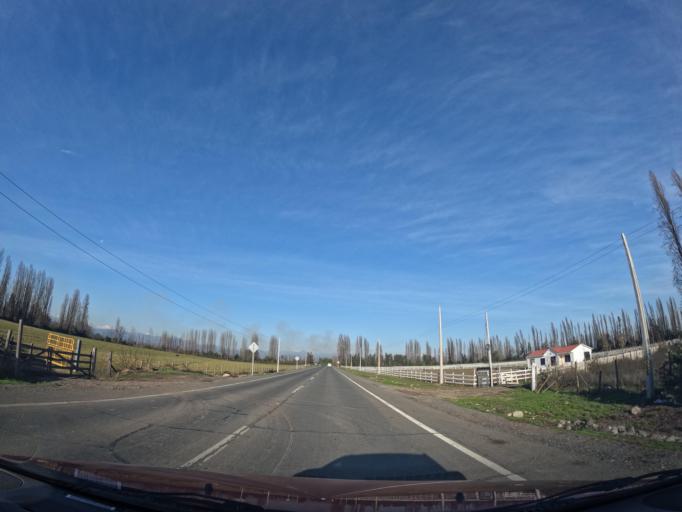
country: CL
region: Maule
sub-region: Provincia de Talca
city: San Clemente
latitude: -35.6250
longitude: -71.4808
